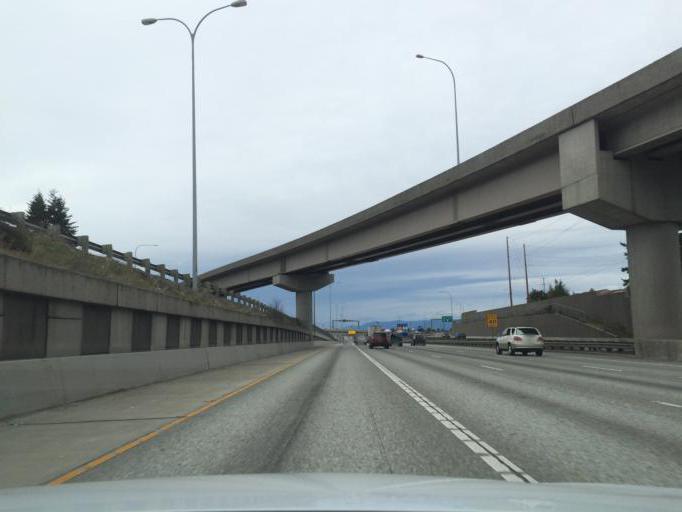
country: US
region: Washington
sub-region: Snohomish County
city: Everett
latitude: 47.9608
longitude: -122.1994
